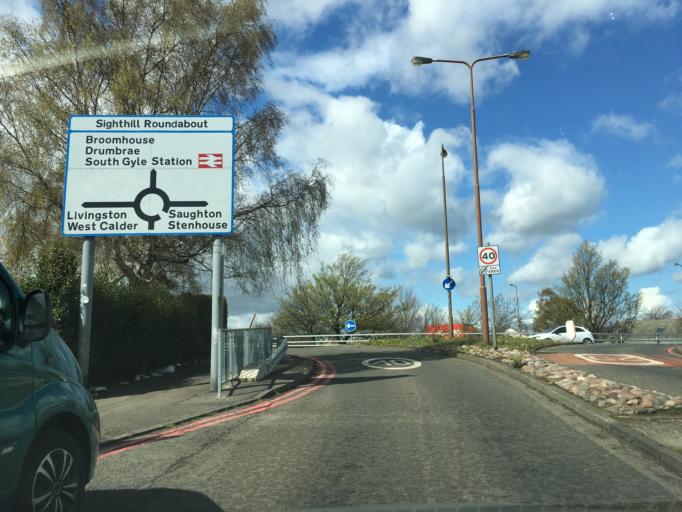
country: GB
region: Scotland
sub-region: Edinburgh
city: Colinton
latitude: 55.9231
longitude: -3.2805
